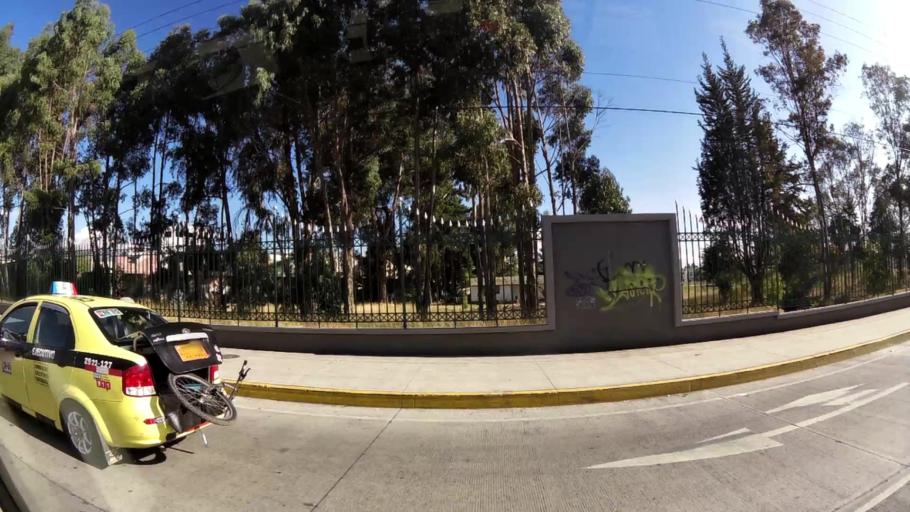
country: EC
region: Chimborazo
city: Riobamba
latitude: -1.6603
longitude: -78.6807
